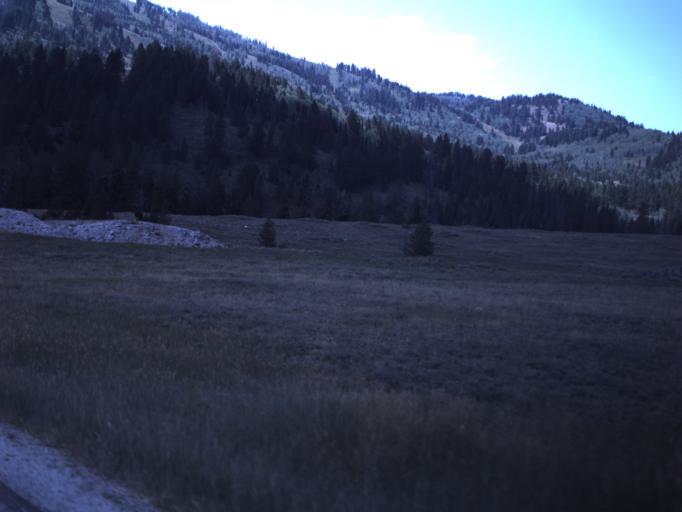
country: US
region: Utah
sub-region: Cache County
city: Richmond
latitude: 41.9645
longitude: -111.5286
